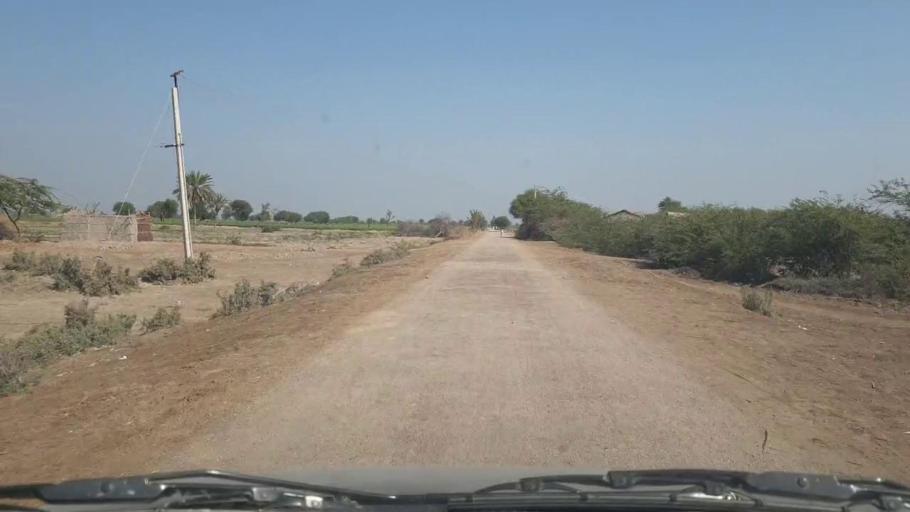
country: PK
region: Sindh
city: Samaro
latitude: 25.2759
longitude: 69.3232
